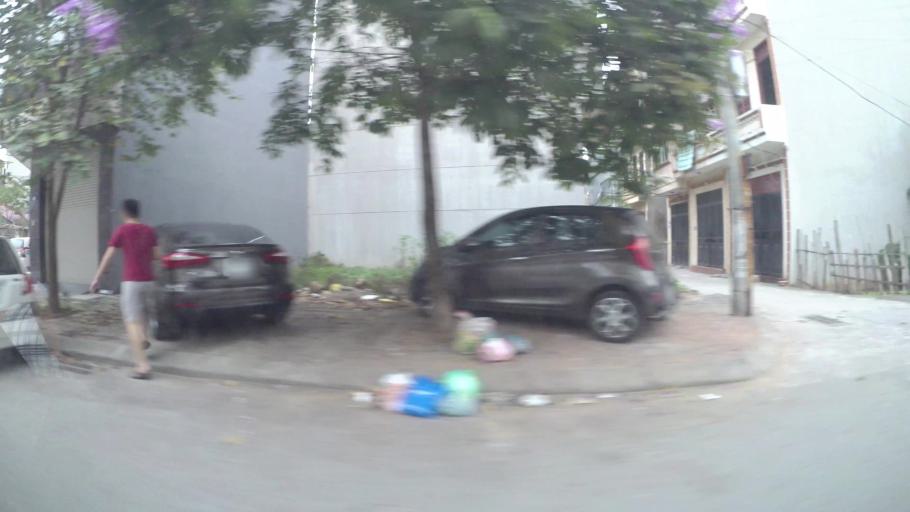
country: VN
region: Ha Noi
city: Hoan Kiem
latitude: 21.0584
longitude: 105.8962
